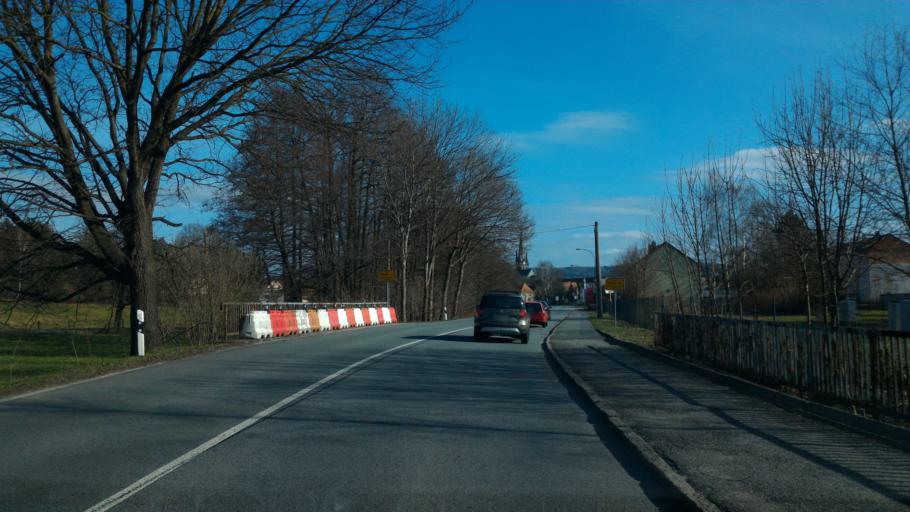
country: DE
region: Saxony
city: Neustadt in Sachsen
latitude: 51.0301
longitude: 14.2065
